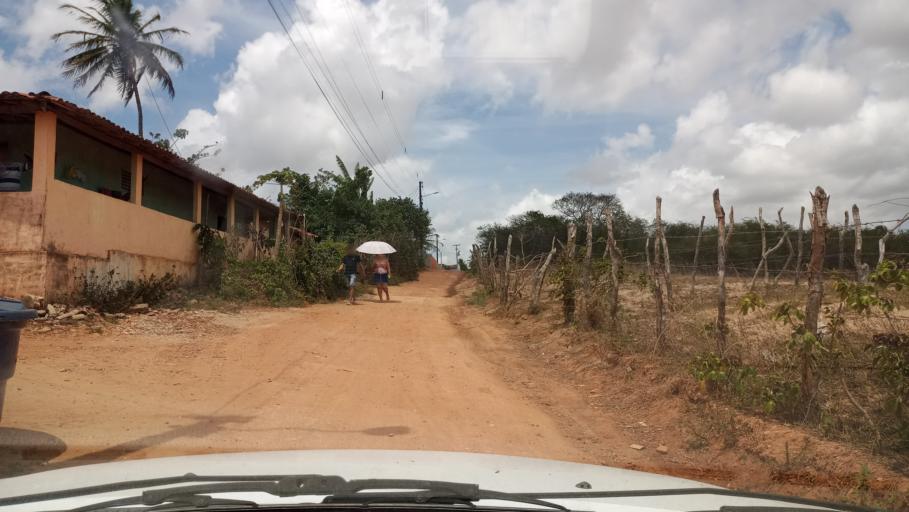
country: BR
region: Rio Grande do Norte
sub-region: Goianinha
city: Goianinha
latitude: -6.2947
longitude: -35.2796
